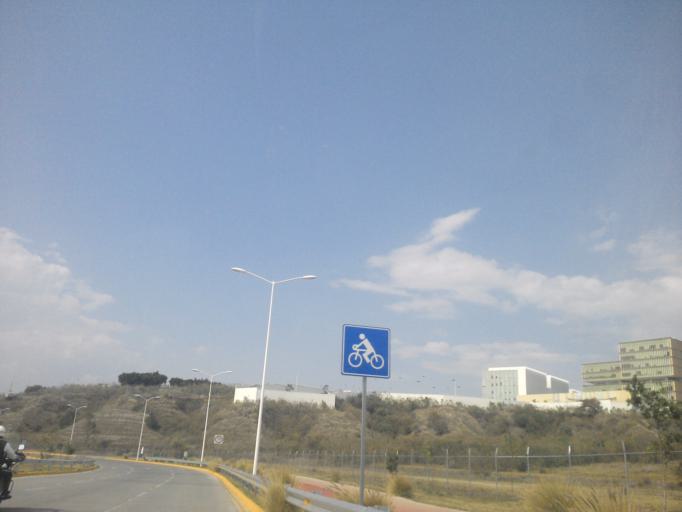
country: MX
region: Jalisco
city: Guadalajara
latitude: 20.6799
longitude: -103.4612
